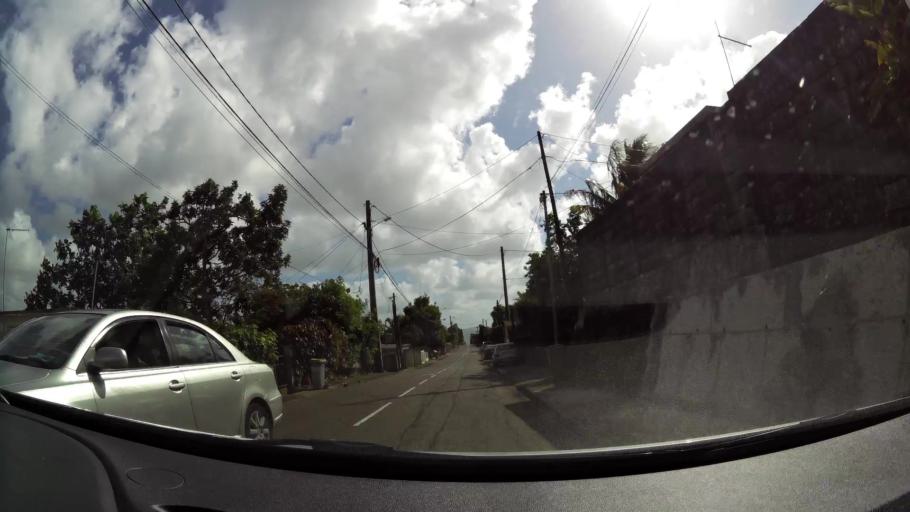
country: MQ
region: Martinique
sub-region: Martinique
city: Fort-de-France
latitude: 14.6376
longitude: -61.0595
